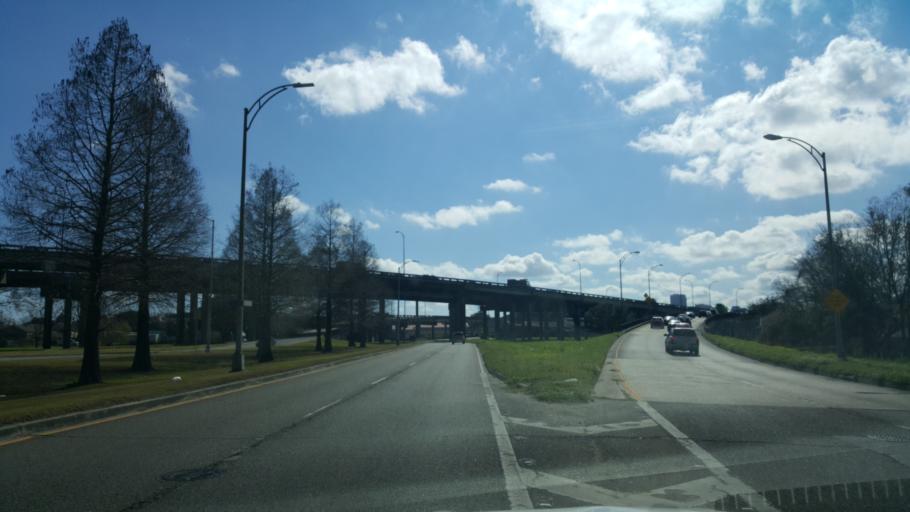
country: US
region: Louisiana
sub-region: Orleans Parish
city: New Orleans
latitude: 29.9820
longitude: -90.0581
